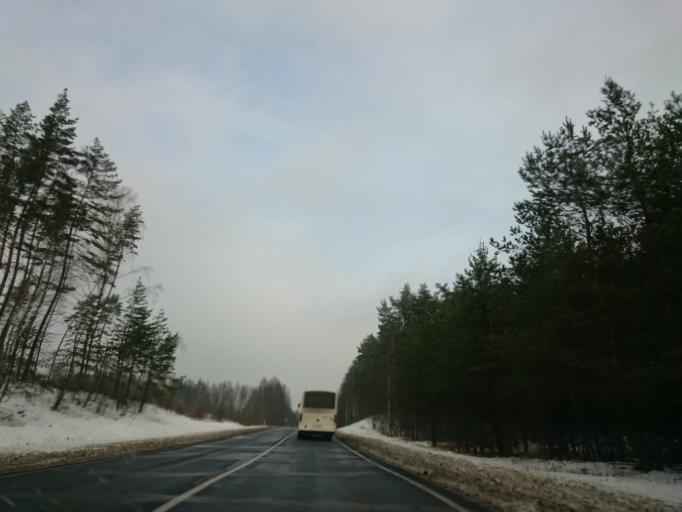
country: LV
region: Pargaujas
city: Stalbe
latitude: 57.3114
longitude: 24.9244
